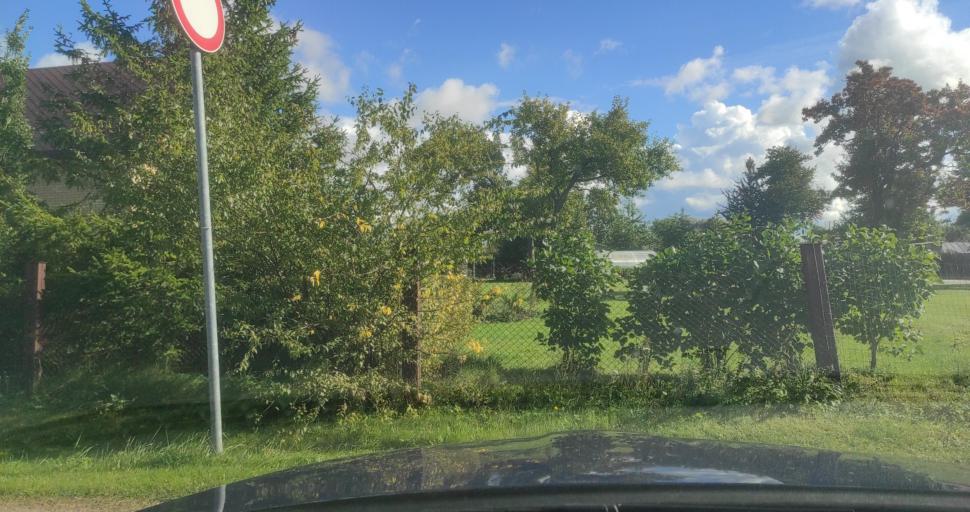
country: LV
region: Ventspils
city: Ventspils
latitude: 57.3714
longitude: 21.6067
